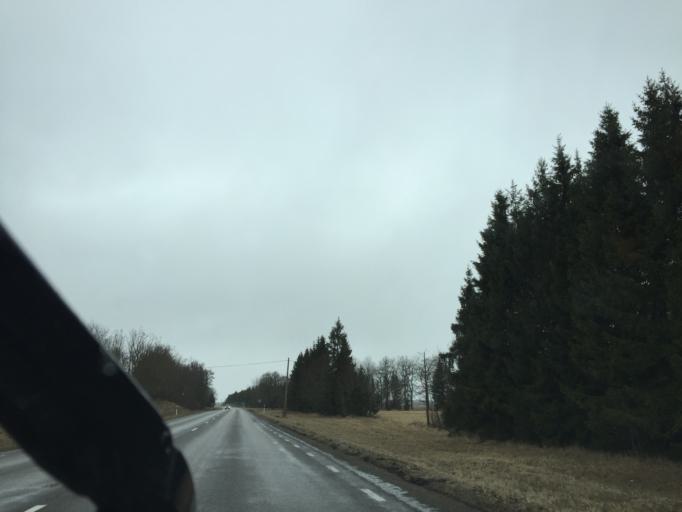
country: EE
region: Laeaene
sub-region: Ridala Parish
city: Uuemoisa
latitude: 58.8765
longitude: 23.6103
